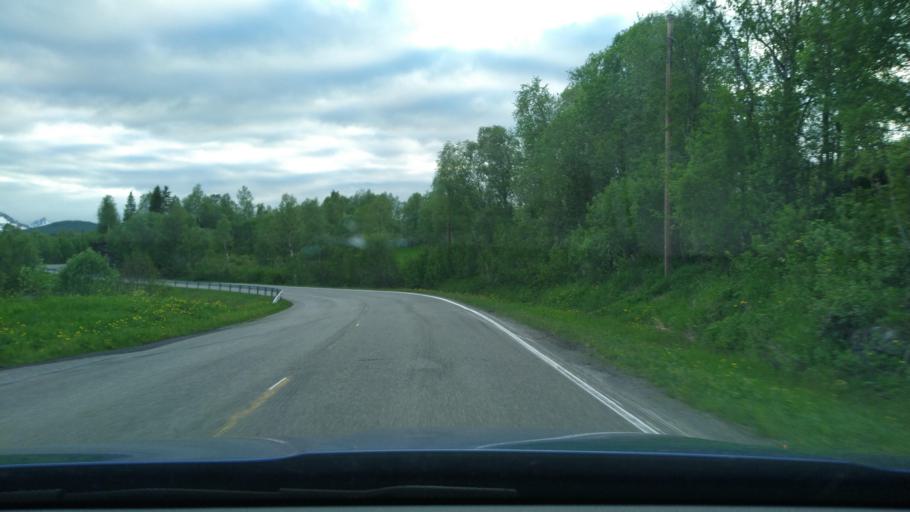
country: NO
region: Troms
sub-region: Sorreisa
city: Sorreisa
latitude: 69.0956
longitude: 18.3354
